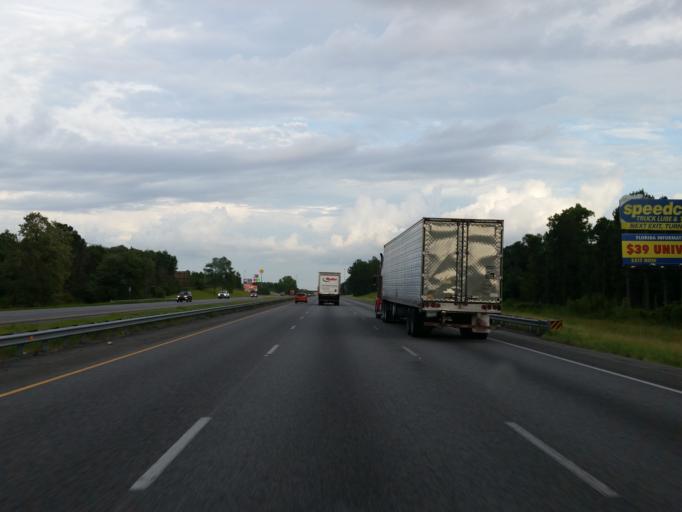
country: US
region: Georgia
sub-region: Echols County
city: Statenville
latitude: 30.6500
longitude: -83.1952
